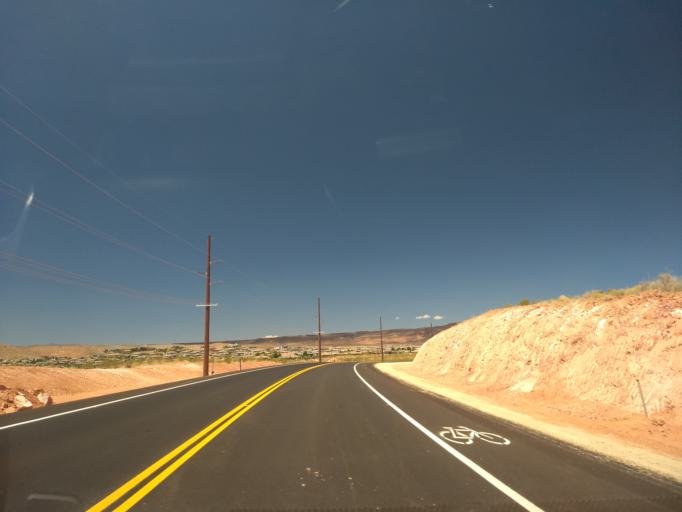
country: US
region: Utah
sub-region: Washington County
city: Washington
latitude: 37.1488
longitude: -113.5142
